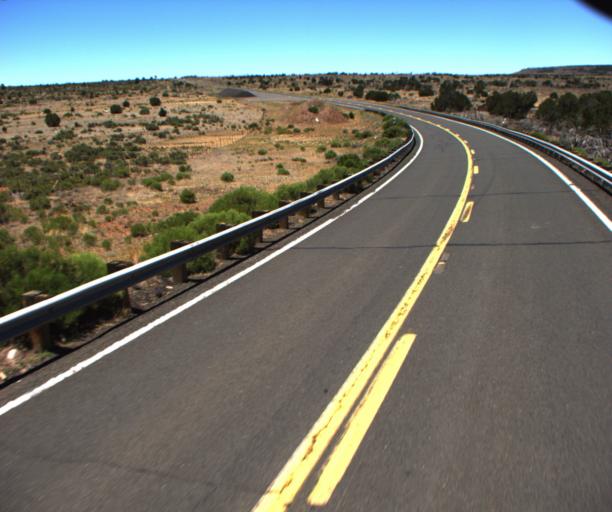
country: US
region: Arizona
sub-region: Coconino County
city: LeChee
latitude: 34.7294
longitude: -111.0785
